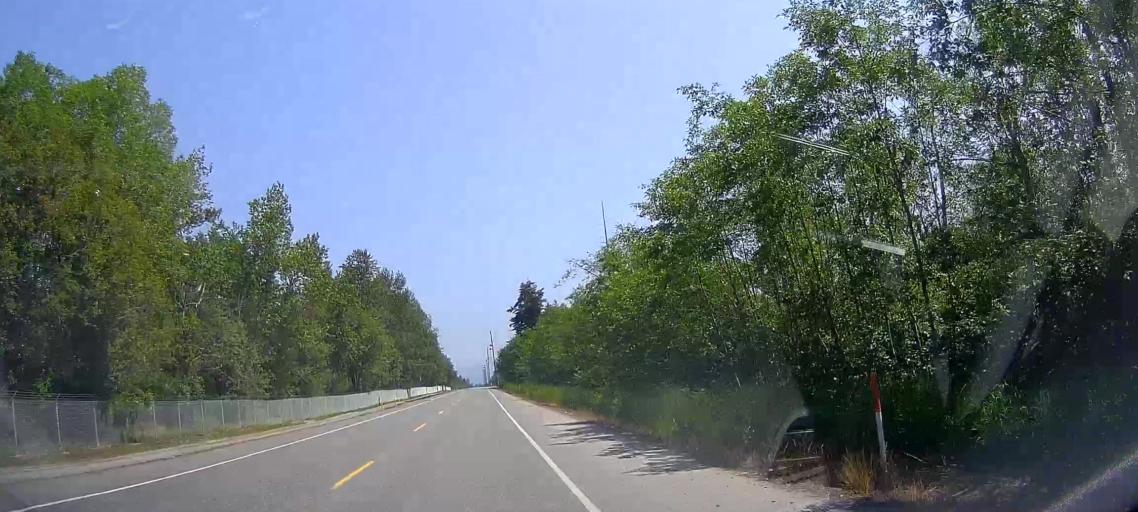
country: US
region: Washington
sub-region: Skagit County
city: Mount Vernon
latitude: 48.4576
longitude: -122.4363
